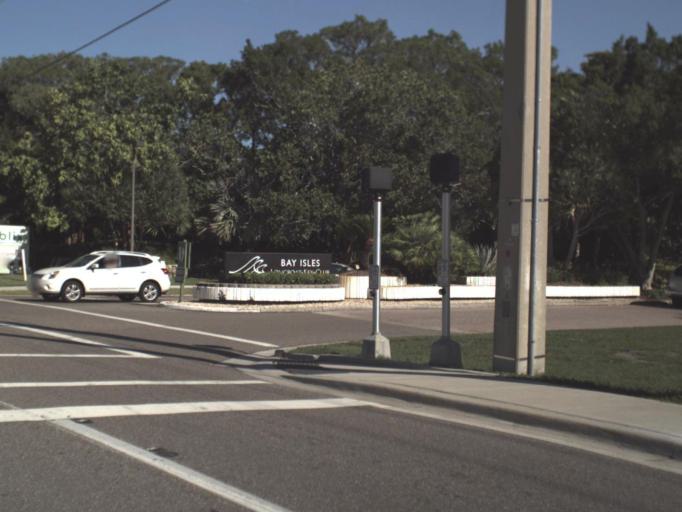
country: US
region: Florida
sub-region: Manatee County
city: Longboat Key
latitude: 27.3652
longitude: -82.6233
